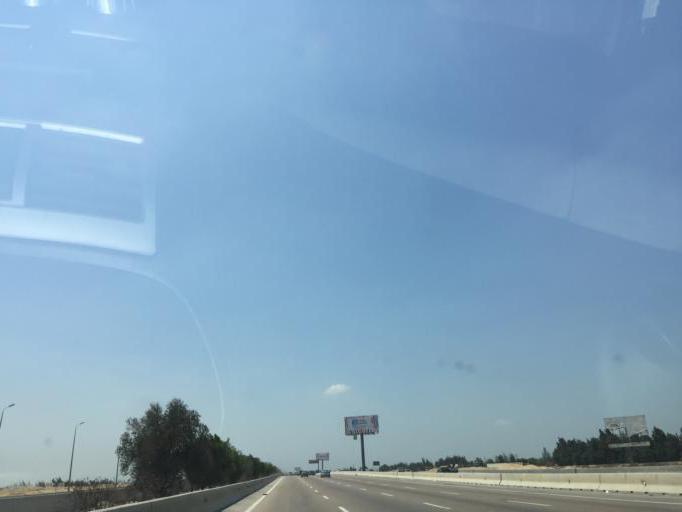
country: EG
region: Al Buhayrah
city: Beheira
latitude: 30.4350
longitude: 30.3347
